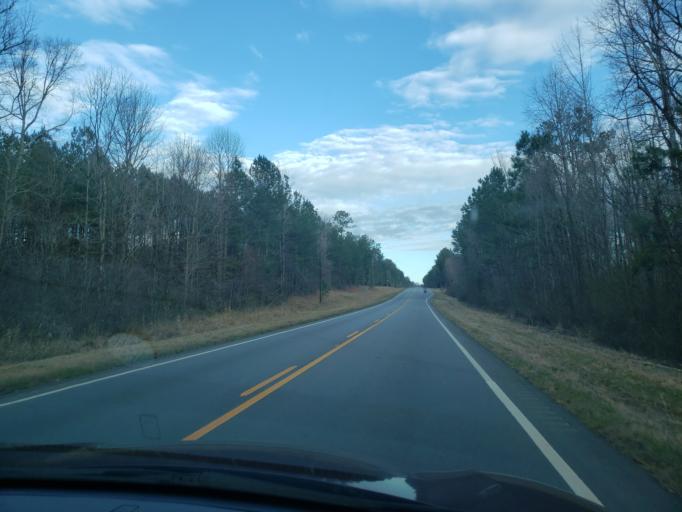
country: US
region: Alabama
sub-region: Randolph County
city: Wedowee
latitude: 33.2402
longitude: -85.4431
